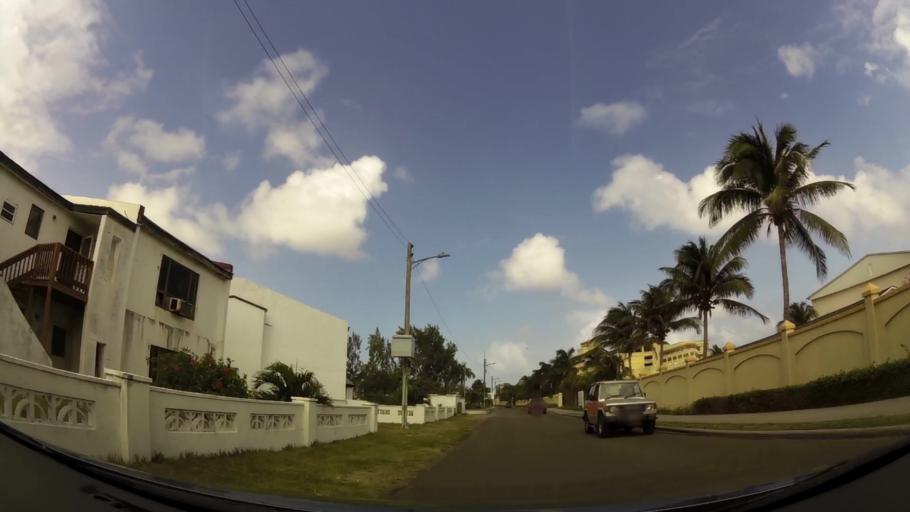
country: KN
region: Saint George Basseterre
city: Basseterre
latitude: 17.2897
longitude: -62.6860
